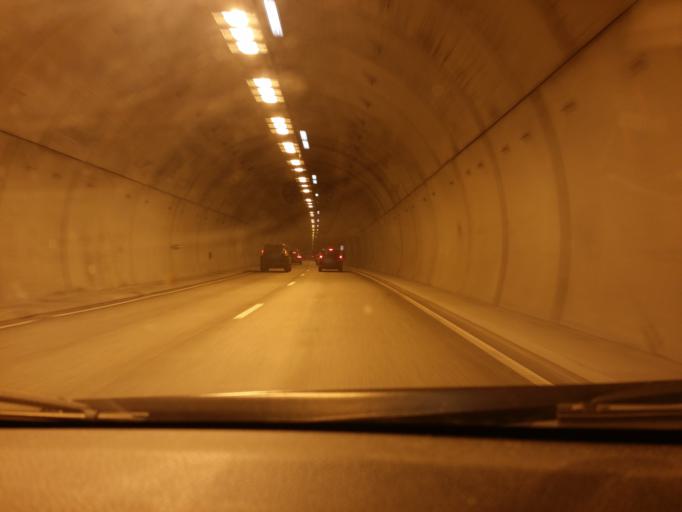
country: NO
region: Akershus
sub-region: Baerum
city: Skui
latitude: 59.9326
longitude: 10.4407
